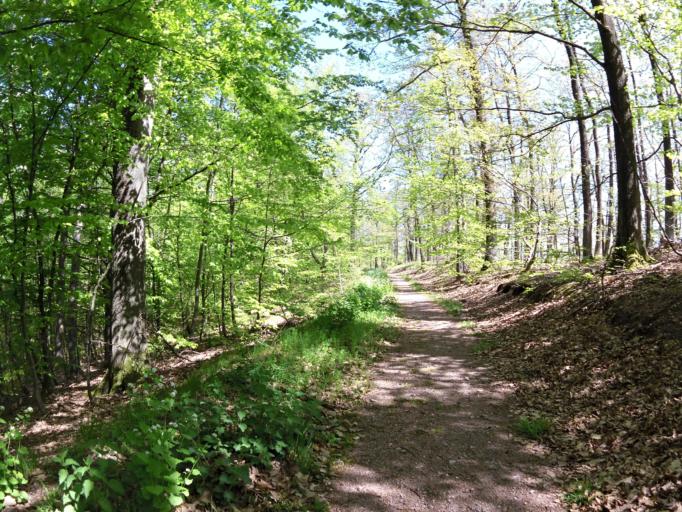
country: DE
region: Thuringia
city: Wolfsburg-Unkeroda
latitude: 50.9628
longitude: 10.2573
